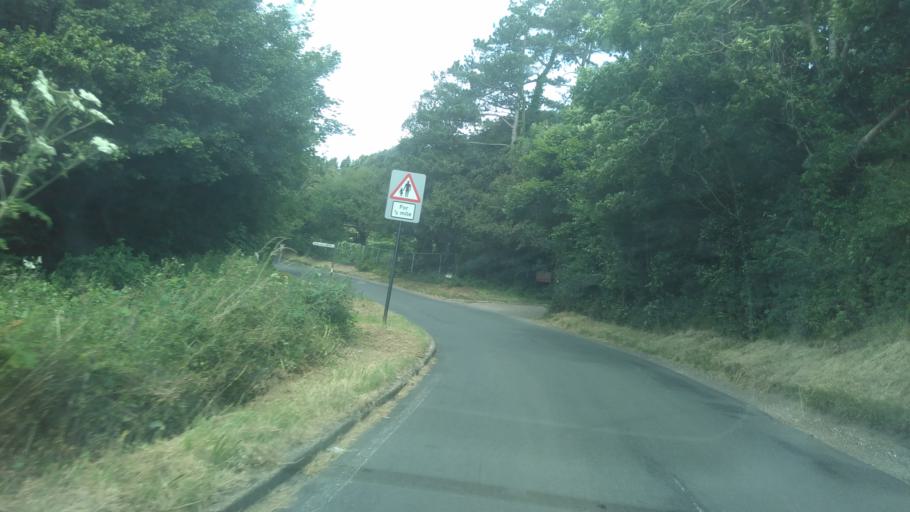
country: GB
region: England
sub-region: Kent
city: Chartham
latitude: 51.2444
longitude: 1.0321
